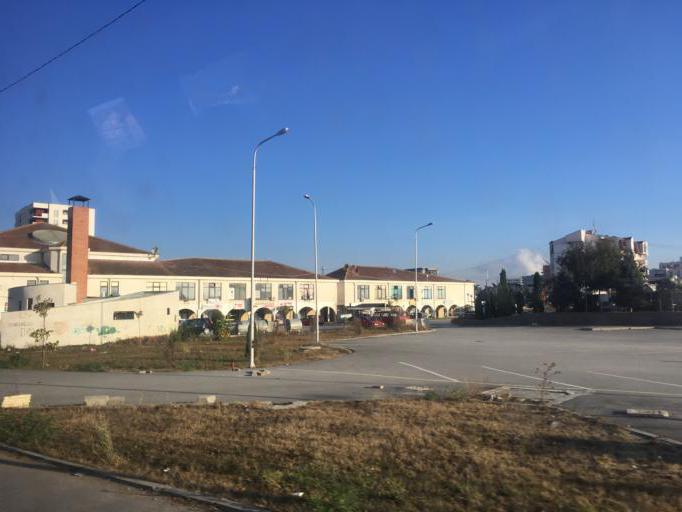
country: XK
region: Pristina
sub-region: Komuna e Drenasit
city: Glogovac
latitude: 42.6201
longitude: 20.8924
